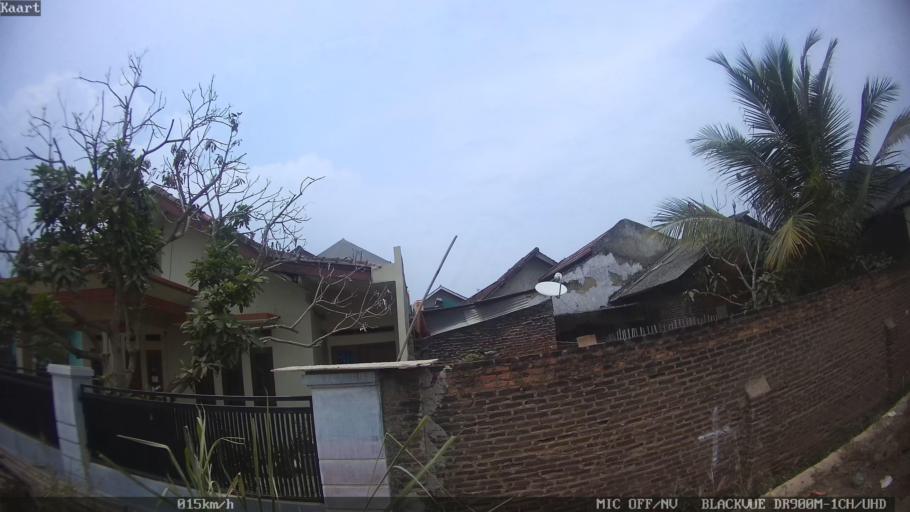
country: ID
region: Lampung
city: Kedaton
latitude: -5.3957
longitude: 105.3207
